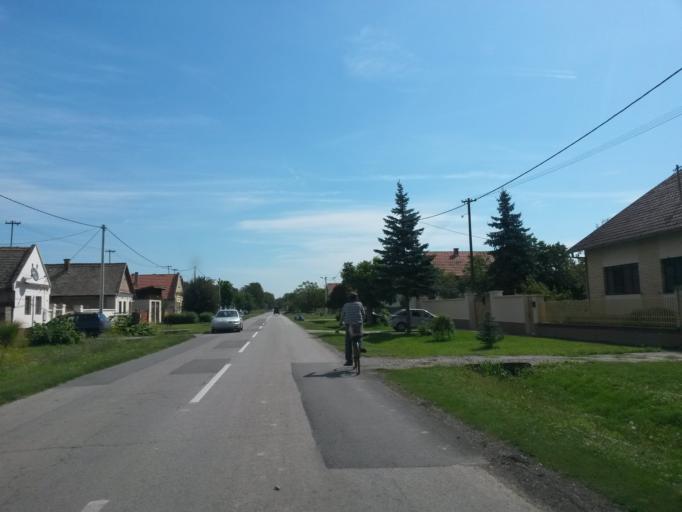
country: HR
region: Vukovarsko-Srijemska
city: Vinkovci
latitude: 45.3405
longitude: 18.7865
